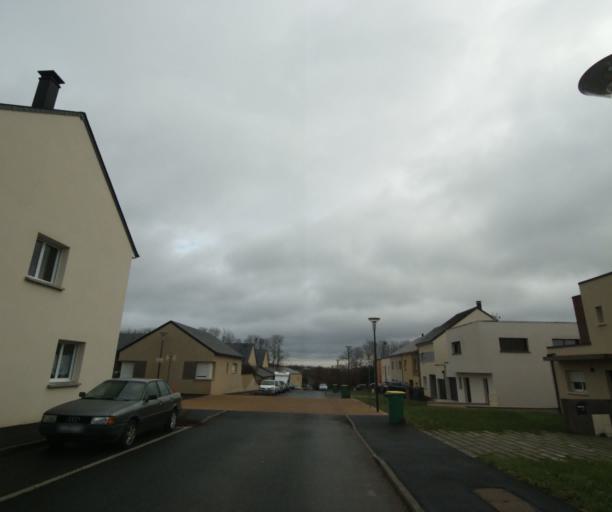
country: FR
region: Pays de la Loire
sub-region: Departement de la Sarthe
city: Rouillon
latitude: 48.0190
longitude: 0.1446
